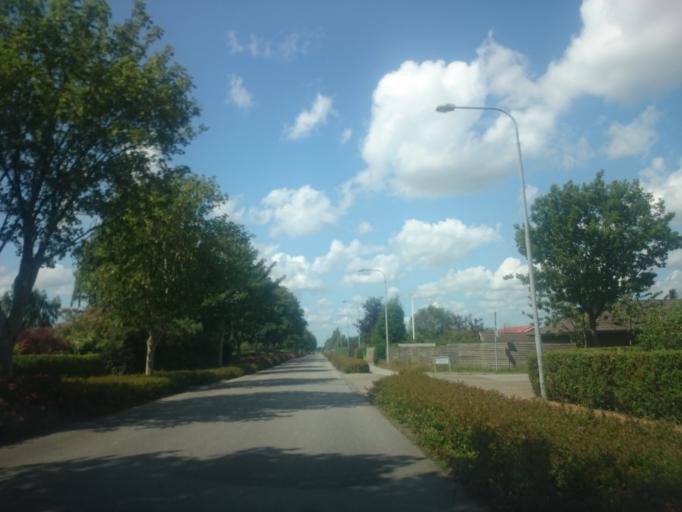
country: DK
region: South Denmark
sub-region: Billund Kommune
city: Billund
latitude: 55.7303
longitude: 9.0978
